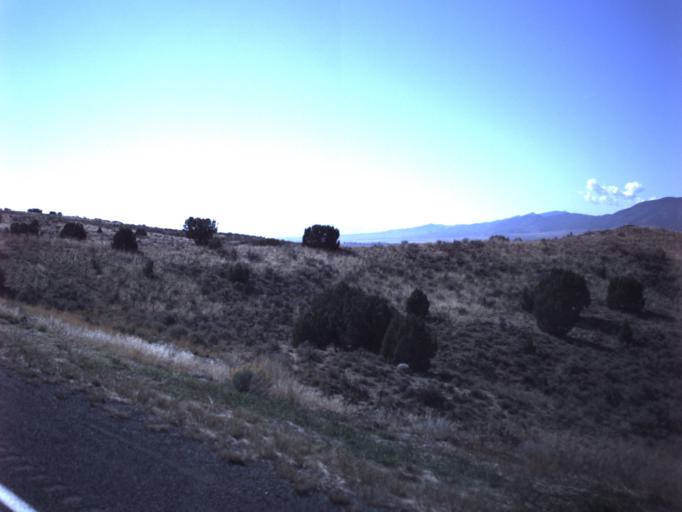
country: US
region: Utah
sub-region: Sanpete County
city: Gunnison
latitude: 39.2823
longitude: -111.8806
